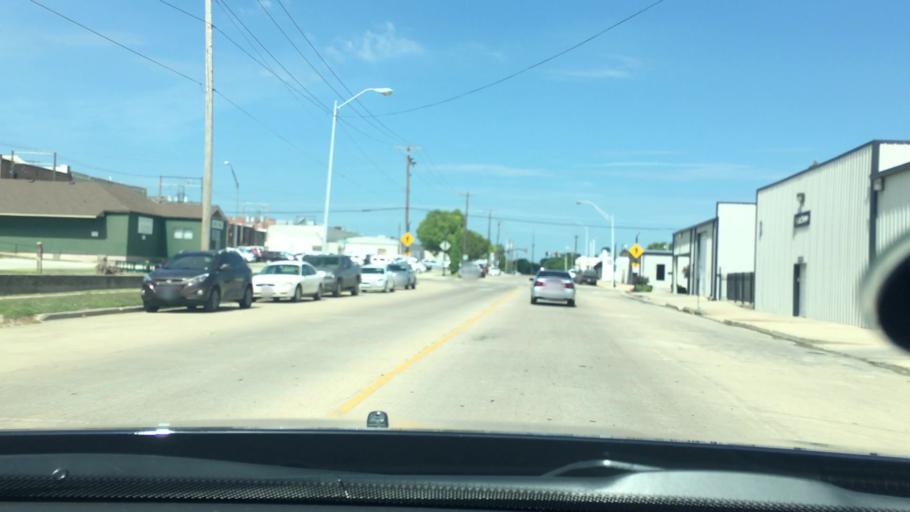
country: US
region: Oklahoma
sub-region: Pontotoc County
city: Ada
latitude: 34.7756
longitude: -96.6760
